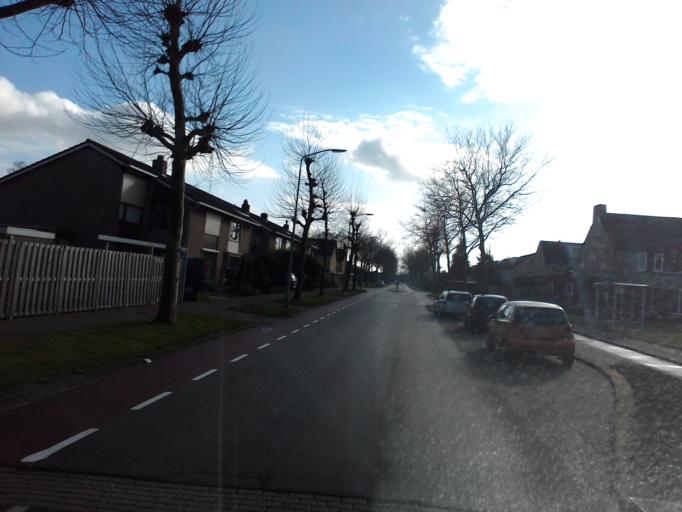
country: NL
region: North Brabant
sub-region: Gemeente Boxtel
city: Boxtel
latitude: 51.5866
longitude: 5.3380
